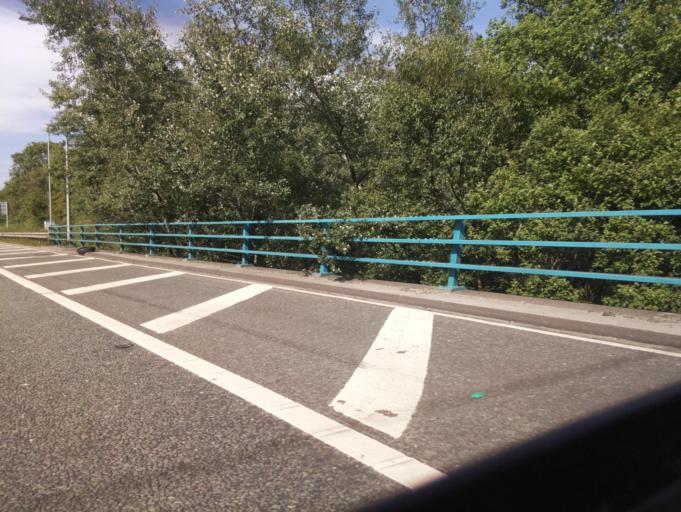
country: GB
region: England
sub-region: Borough of Bolton
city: Kearsley
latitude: 53.5142
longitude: -2.3696
